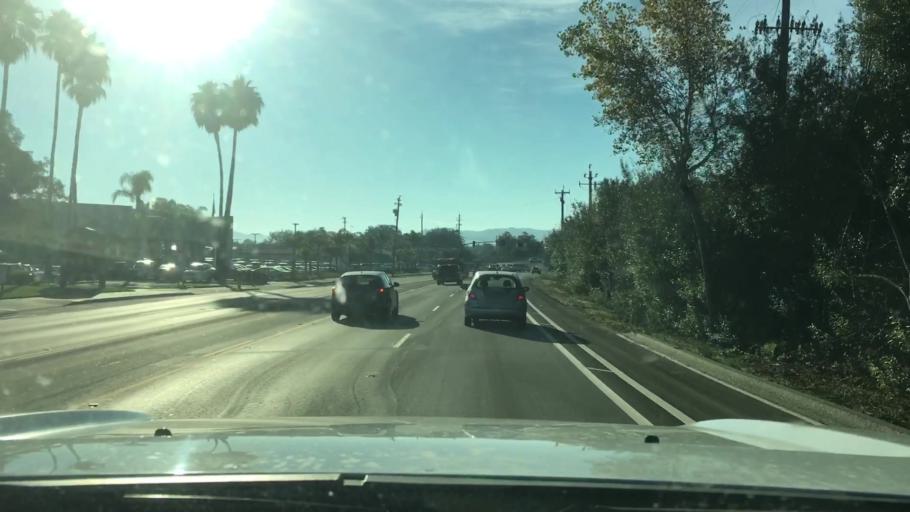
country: US
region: California
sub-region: San Luis Obispo County
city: San Luis Obispo
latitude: 35.2485
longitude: -120.6841
